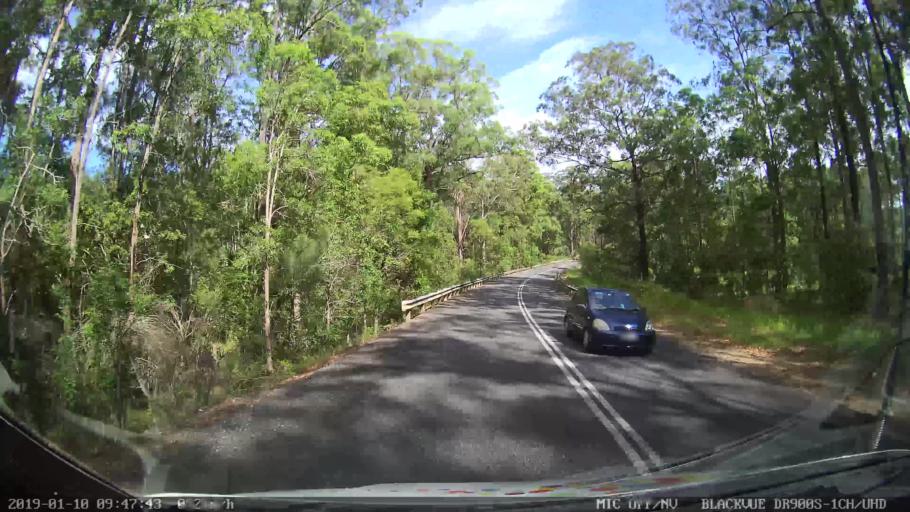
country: AU
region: New South Wales
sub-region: Coffs Harbour
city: Nana Glen
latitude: -30.0816
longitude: 152.9902
